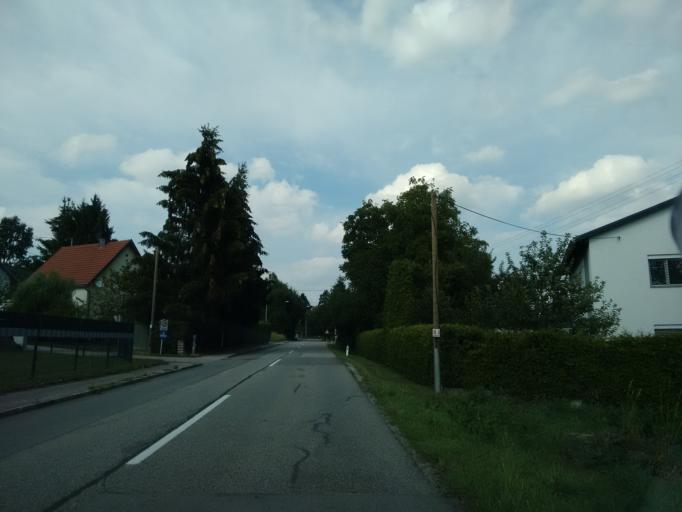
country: AT
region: Upper Austria
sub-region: Politischer Bezirk Grieskirchen
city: Bad Schallerbach
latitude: 48.2365
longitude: 13.9530
